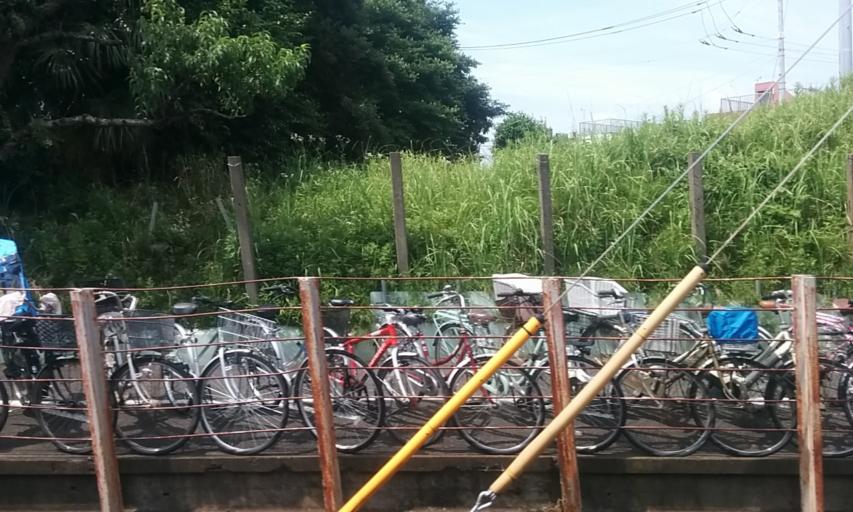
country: JP
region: Chiba
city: Funabashi
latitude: 35.7054
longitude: 139.9725
